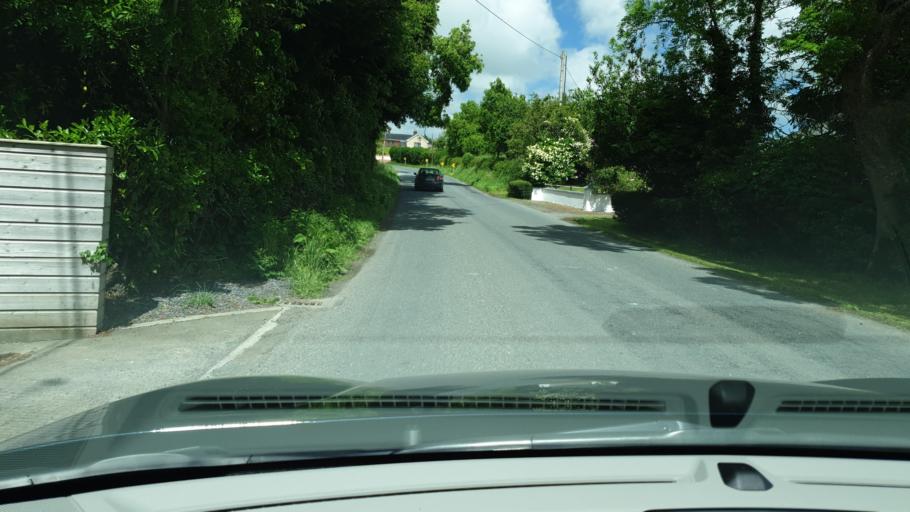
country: IE
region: Leinster
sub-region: Lu
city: Ardee
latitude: 53.7969
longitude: -6.6359
